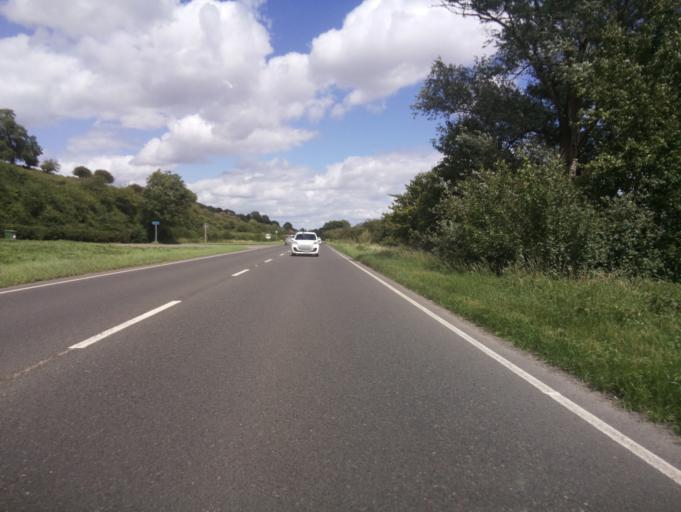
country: GB
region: England
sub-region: Nottinghamshire
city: Lowdham
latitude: 53.0013
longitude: -1.0138
